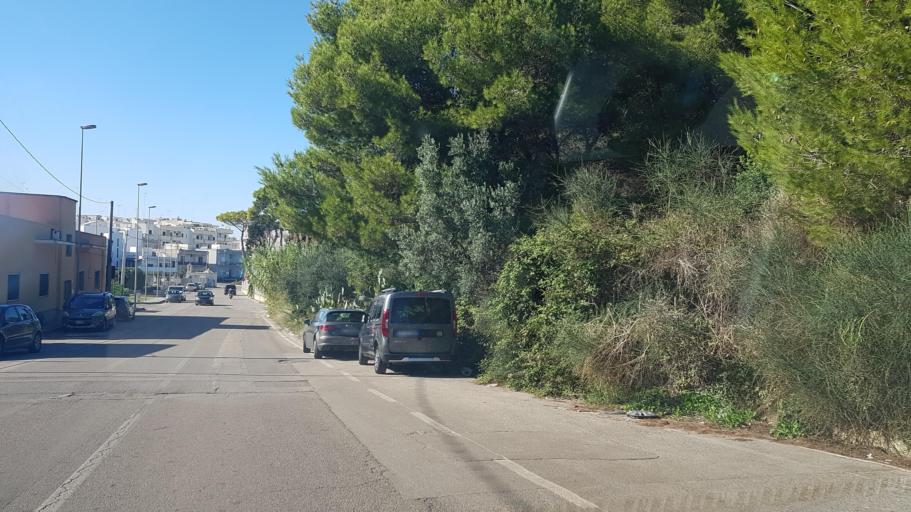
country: IT
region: Apulia
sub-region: Provincia di Lecce
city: Otranto
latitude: 40.1427
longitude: 18.4966
